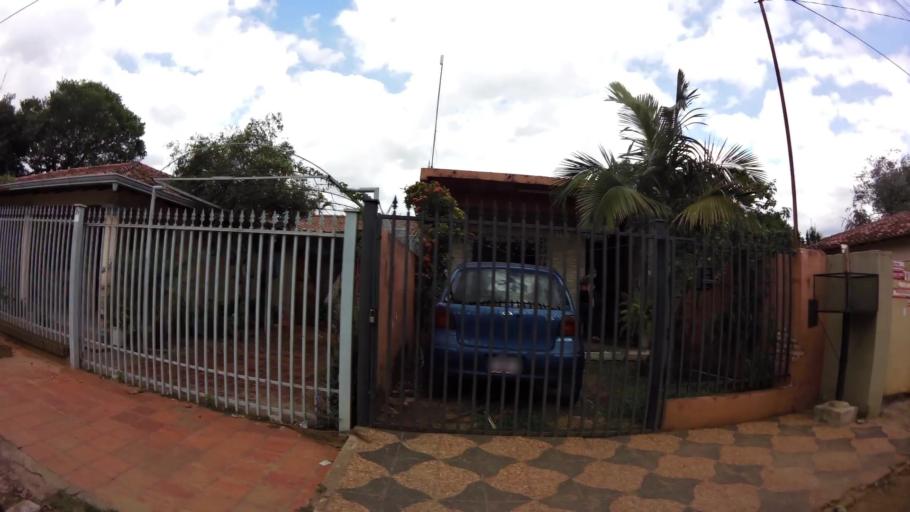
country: PY
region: Central
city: San Lorenzo
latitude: -25.2757
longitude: -57.4892
